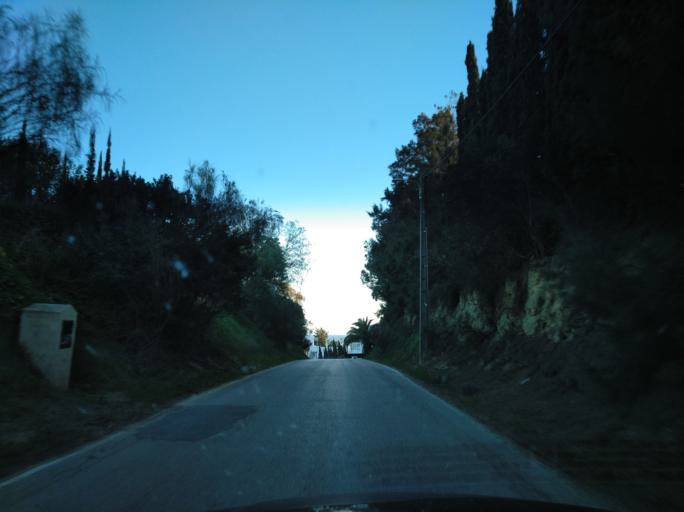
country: PT
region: Faro
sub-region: Tavira
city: Tavira
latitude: 37.1557
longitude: -7.5536
